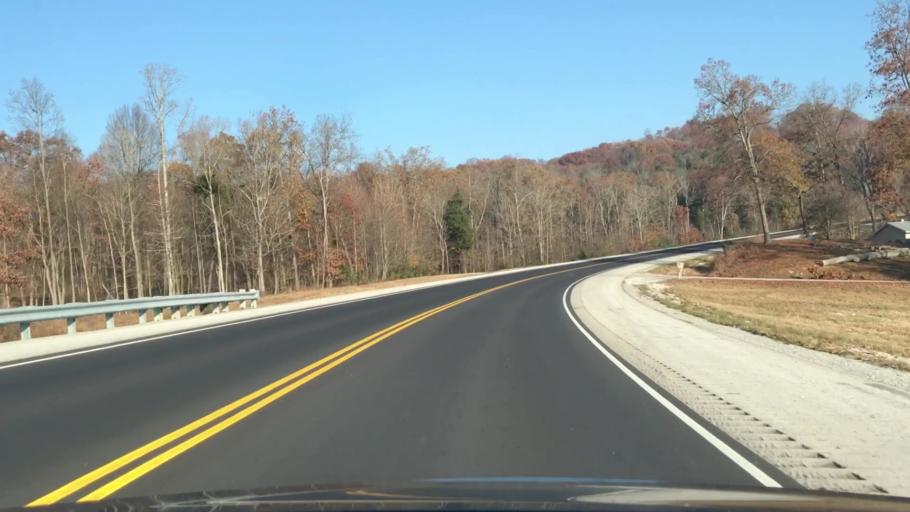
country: US
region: Kentucky
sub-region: Edmonson County
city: Brownsville
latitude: 37.0928
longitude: -86.2335
